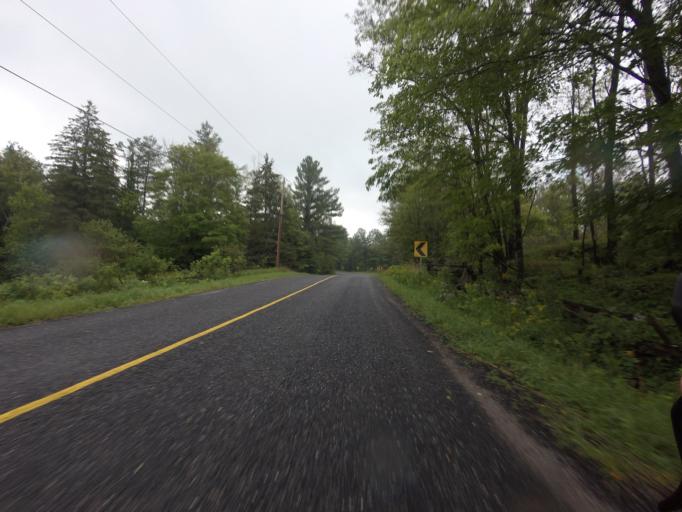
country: CA
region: Ontario
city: Perth
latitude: 45.0629
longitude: -76.5395
